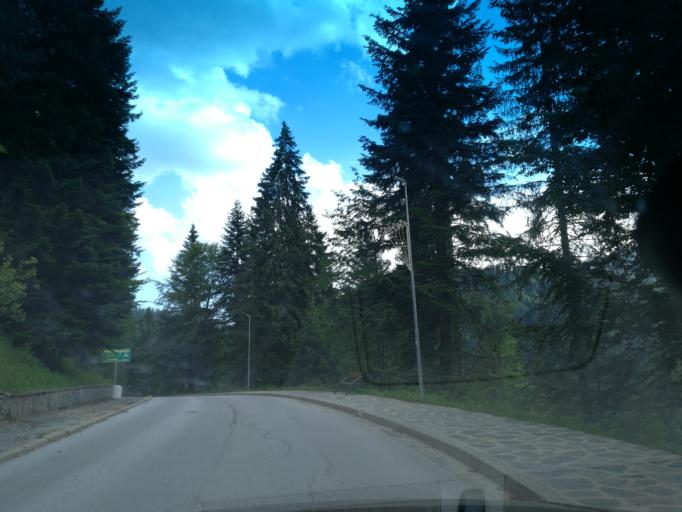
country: BG
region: Smolyan
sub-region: Obshtina Smolyan
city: Smolyan
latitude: 41.6543
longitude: 24.6917
